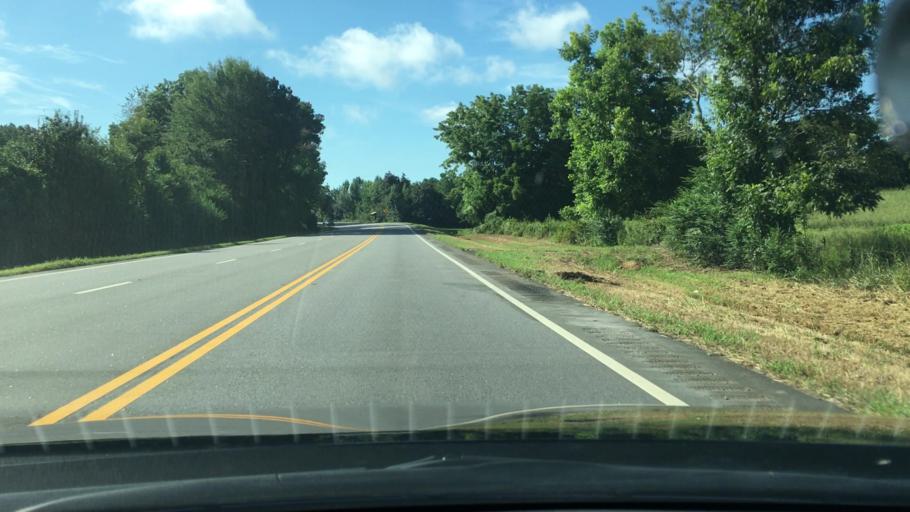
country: US
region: Georgia
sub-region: Morgan County
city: Madison
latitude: 33.4779
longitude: -83.4330
